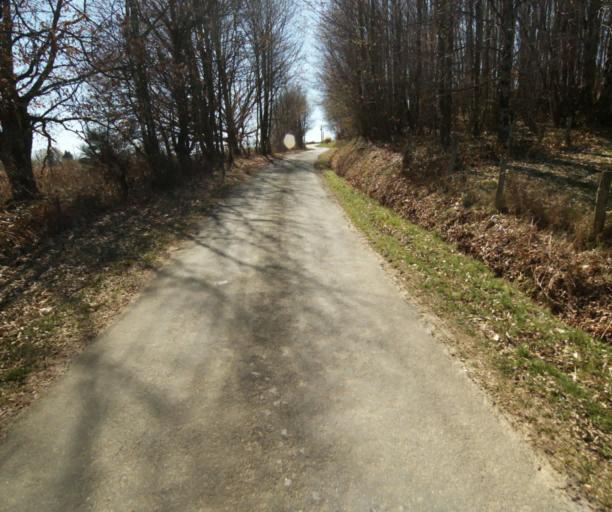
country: FR
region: Limousin
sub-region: Departement de la Correze
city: Saint-Clement
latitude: 45.3137
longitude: 1.6981
